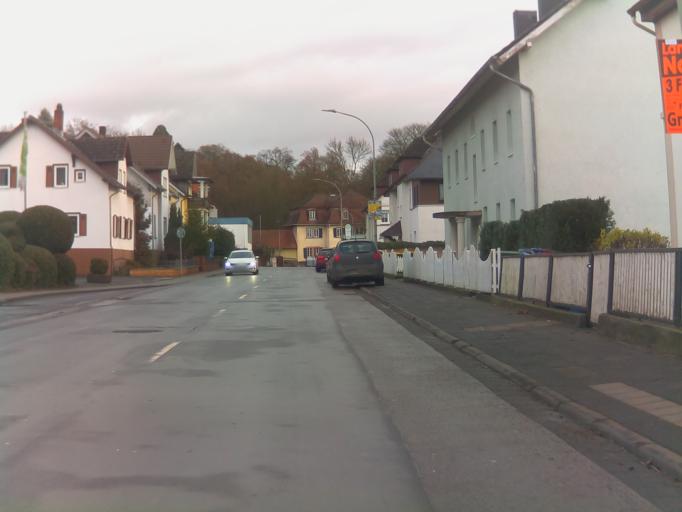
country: DE
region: Hesse
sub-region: Regierungsbezirk Giessen
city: Laubach
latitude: 50.5449
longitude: 8.9854
